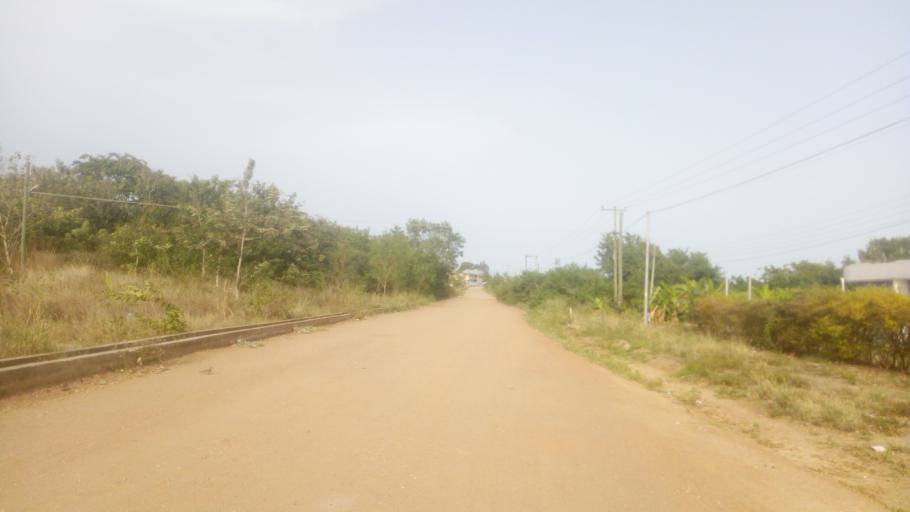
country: GH
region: Central
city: Winneba
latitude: 5.3765
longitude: -0.6375
